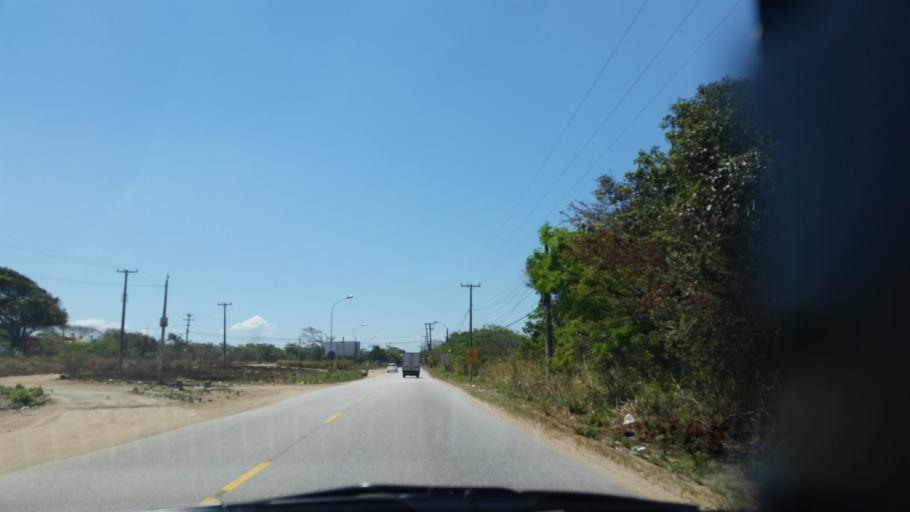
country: BR
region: Rio de Janeiro
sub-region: Cabo Frio
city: Cabo Frio
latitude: -22.8361
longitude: -41.9933
